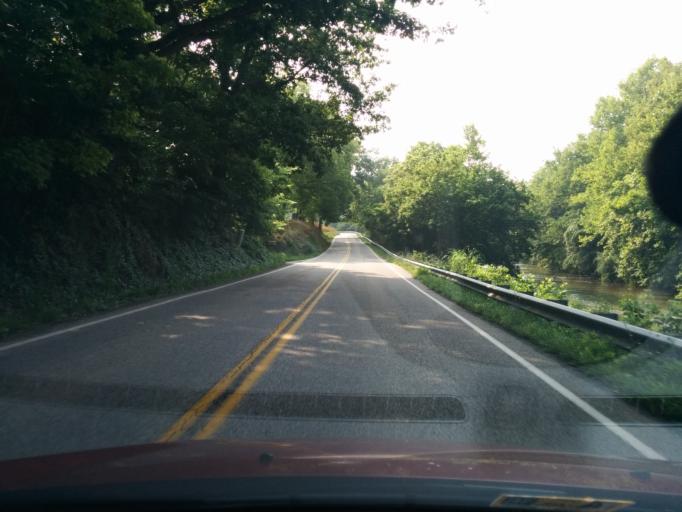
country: US
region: Virginia
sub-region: City of Lexington
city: Lexington
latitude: 37.7452
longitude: -79.5116
